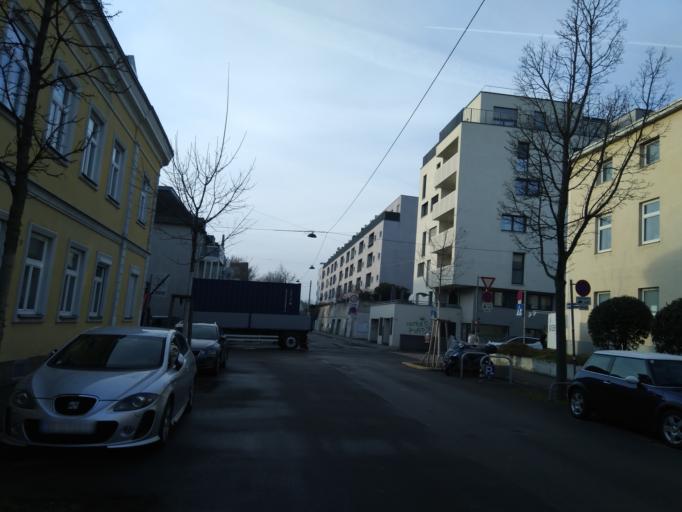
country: AT
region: Lower Austria
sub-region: Politischer Bezirk Modling
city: Perchtoldsdorf
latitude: 48.1424
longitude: 16.2893
